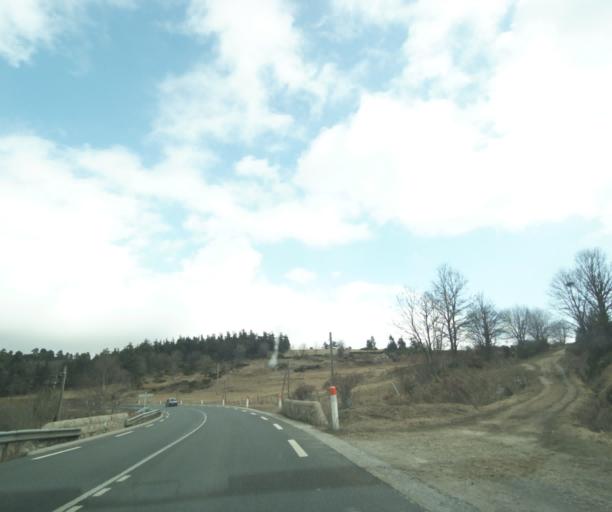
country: FR
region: Languedoc-Roussillon
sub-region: Departement de la Lozere
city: Mende
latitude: 44.5998
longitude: 3.6699
